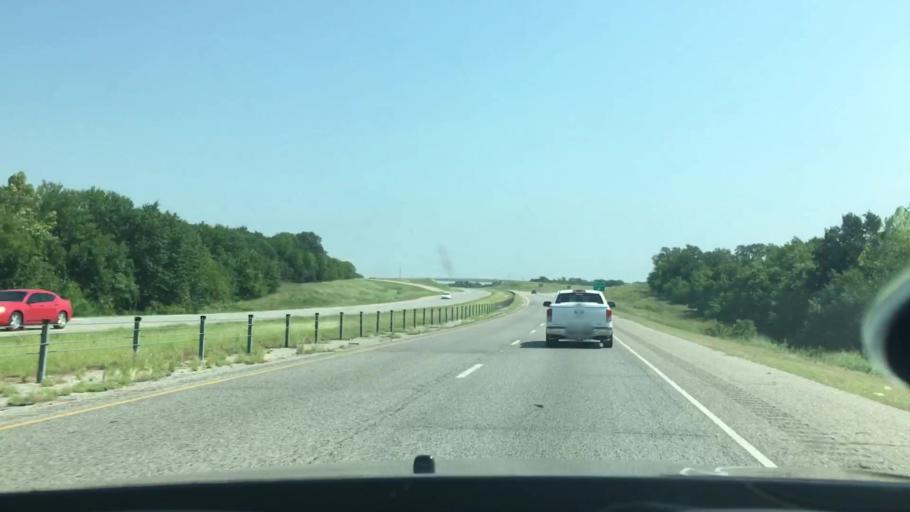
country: US
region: Oklahoma
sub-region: Bryan County
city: Durant
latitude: 34.0460
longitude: -96.3626
